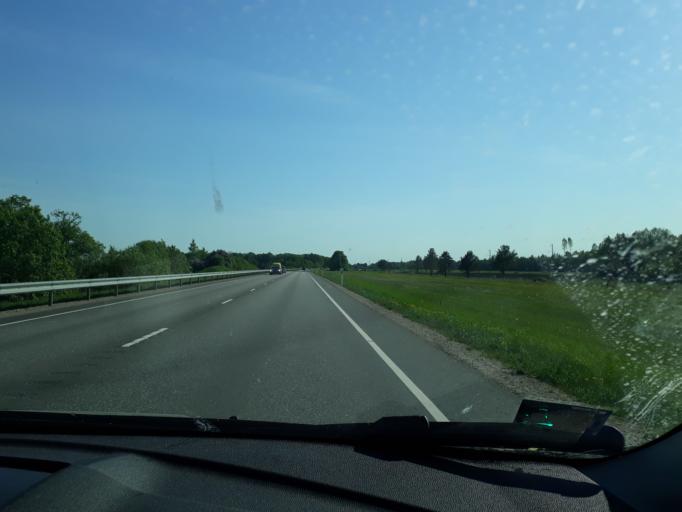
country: EE
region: Paernumaa
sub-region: Tootsi vald
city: Tootsi
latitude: 58.5828
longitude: 24.8941
